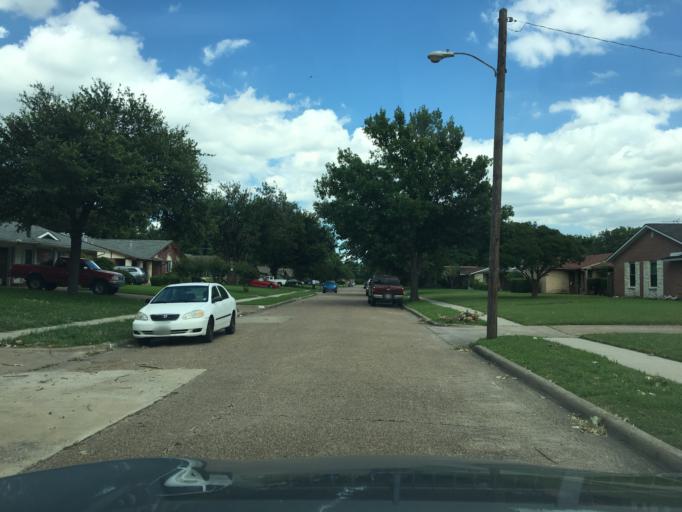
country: US
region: Texas
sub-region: Dallas County
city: Richardson
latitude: 32.9466
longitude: -96.7084
